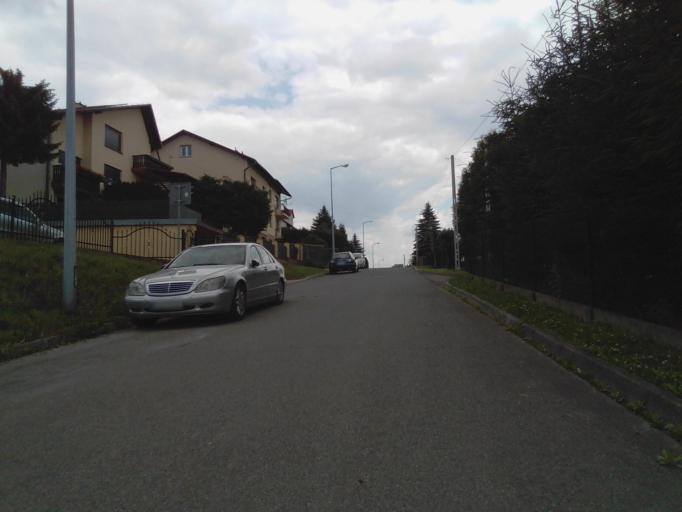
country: PL
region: Subcarpathian Voivodeship
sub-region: Powiat strzyzowski
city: Strzyzow
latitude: 49.8783
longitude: 21.7708
